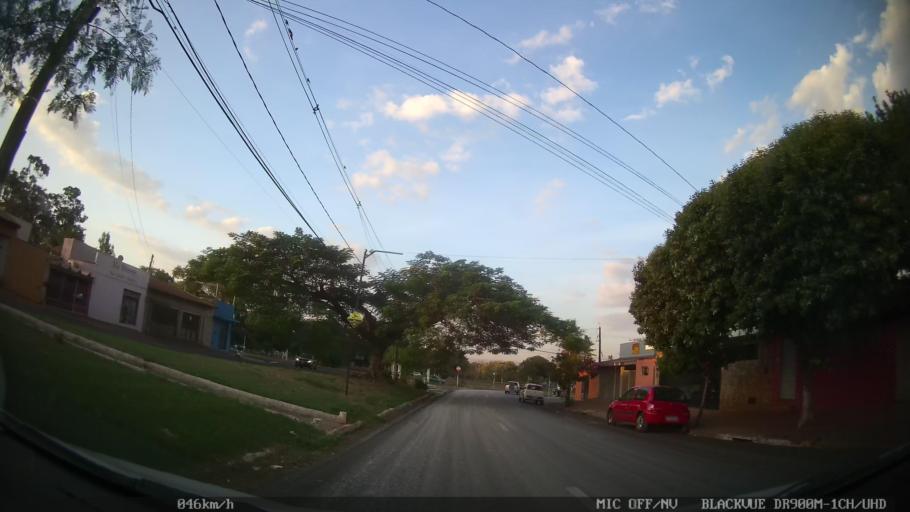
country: BR
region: Sao Paulo
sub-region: Ribeirao Preto
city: Ribeirao Preto
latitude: -21.1326
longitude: -47.8416
